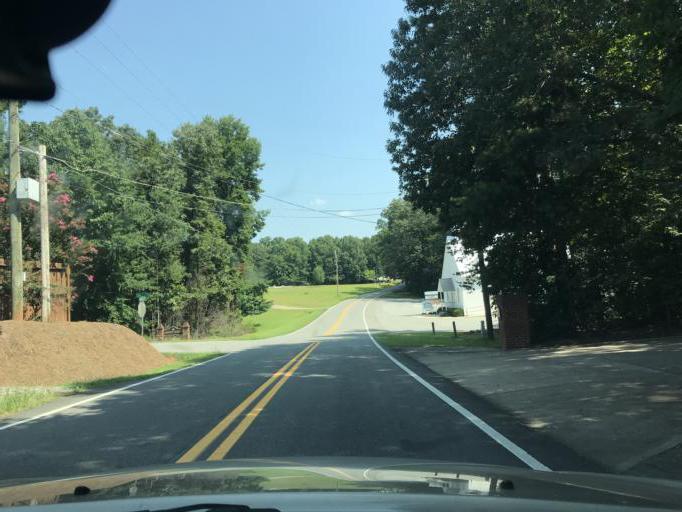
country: US
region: Georgia
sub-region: Hall County
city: Flowery Branch
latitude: 34.2253
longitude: -84.0056
